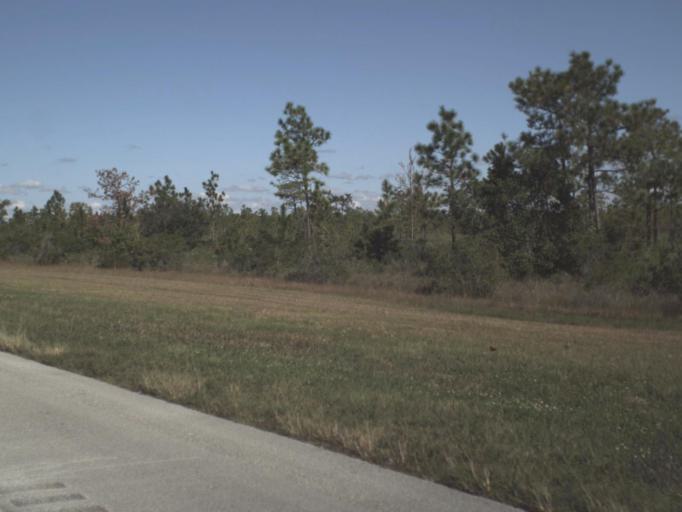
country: US
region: Florida
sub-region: Osceola County
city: Saint Cloud
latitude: 27.9875
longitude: -81.1253
